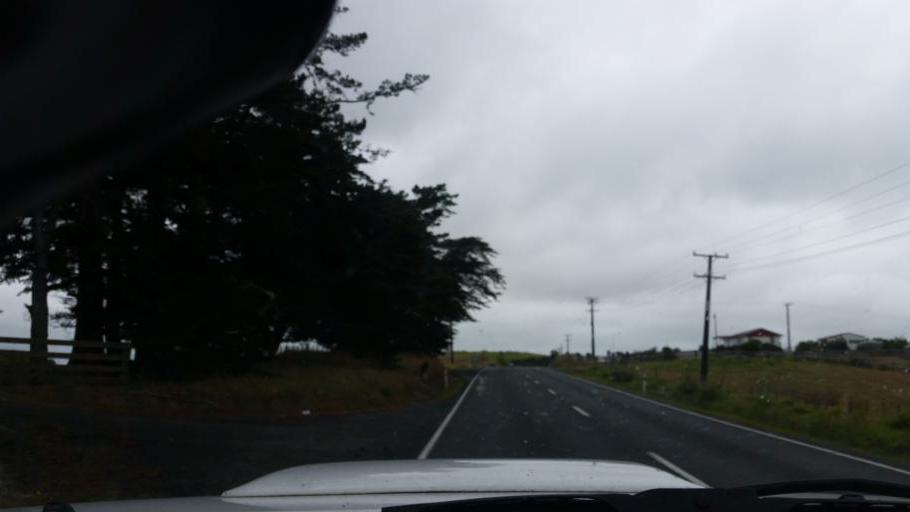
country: NZ
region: Auckland
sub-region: Auckland
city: Wellsford
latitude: -36.1444
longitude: 174.4916
